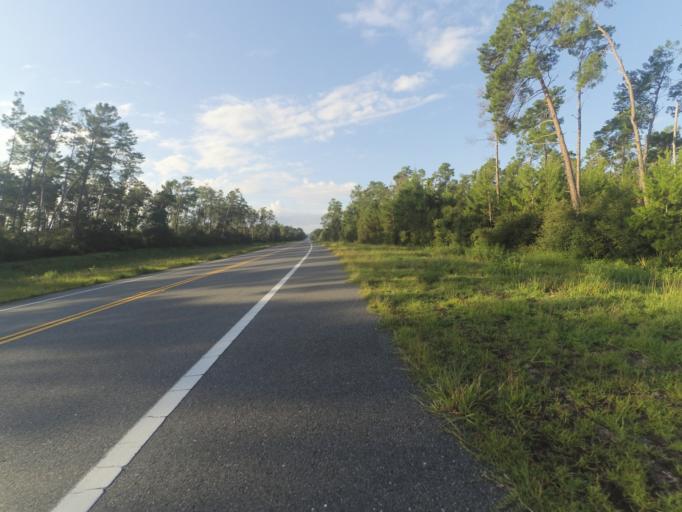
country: US
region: Florida
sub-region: Lake County
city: Astor
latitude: 29.2062
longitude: -81.6598
